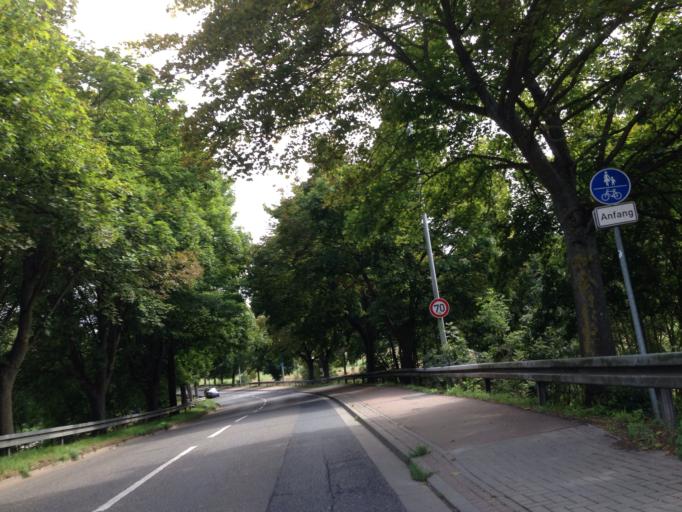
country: DE
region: Hesse
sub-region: Regierungsbezirk Giessen
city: Limburg an der Lahn
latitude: 50.3935
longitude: 8.0398
